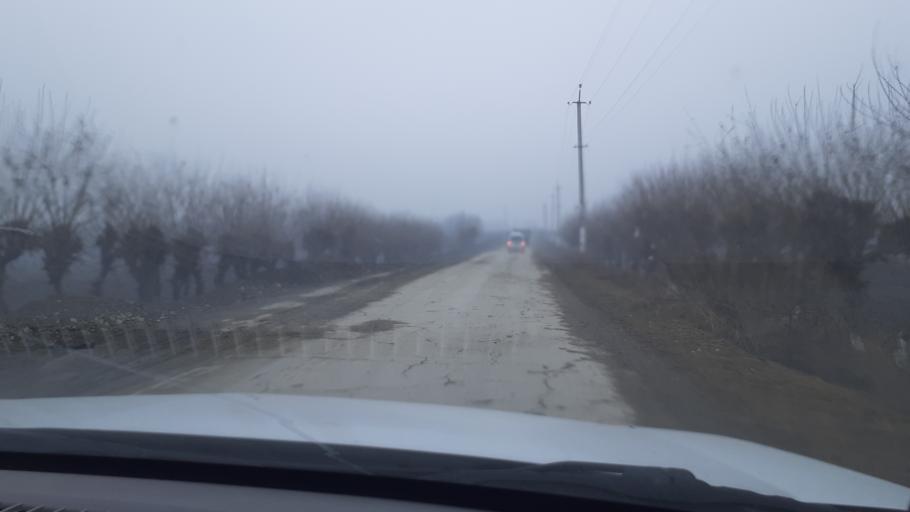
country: UZ
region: Namangan
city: Haqqulobod
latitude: 40.9001
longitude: 72.0003
